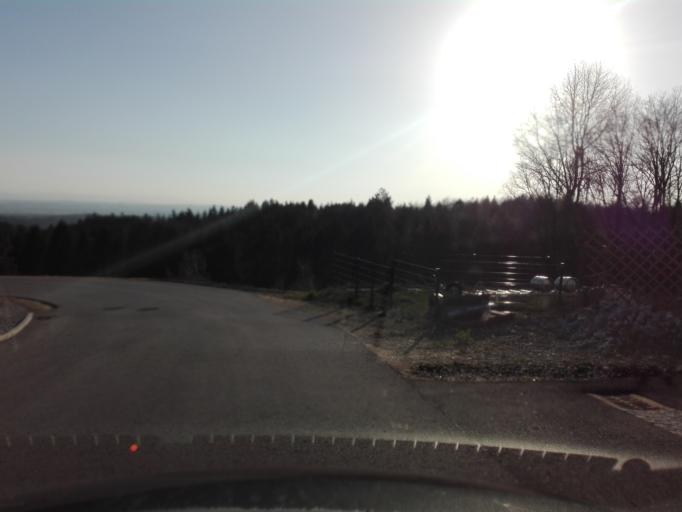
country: AT
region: Upper Austria
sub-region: Politischer Bezirk Perg
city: Perg
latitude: 48.2670
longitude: 14.7053
